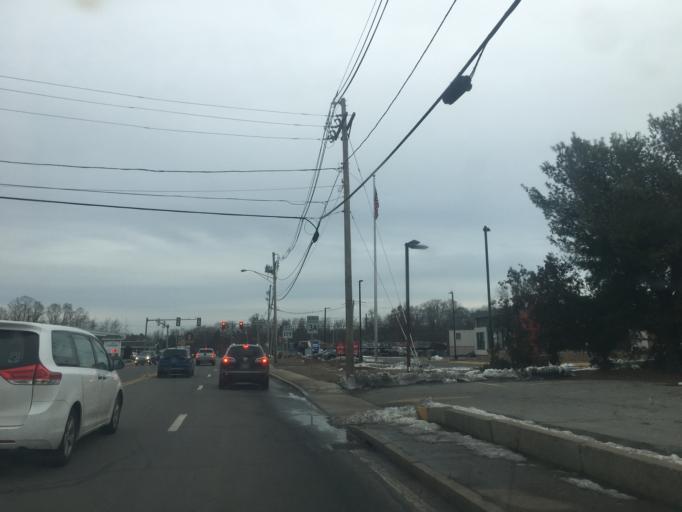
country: US
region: Massachusetts
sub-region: Middlesex County
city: Billerica
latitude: 42.5714
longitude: -71.2771
